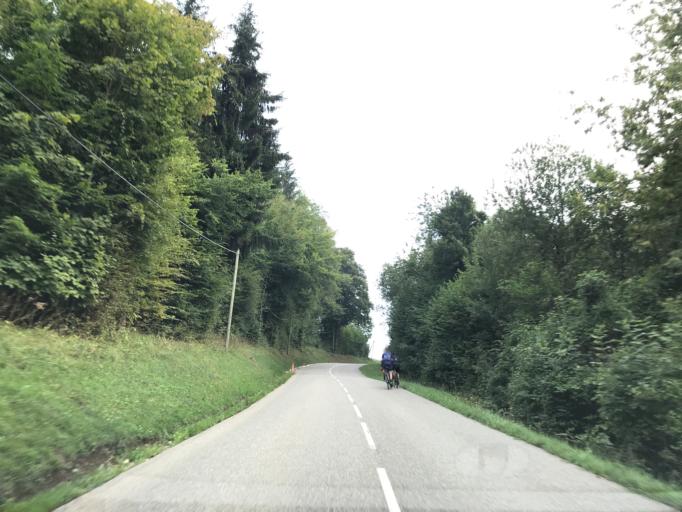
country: FR
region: Rhone-Alpes
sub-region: Departement de la Haute-Savoie
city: Talloires
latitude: 45.8247
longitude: 6.2372
